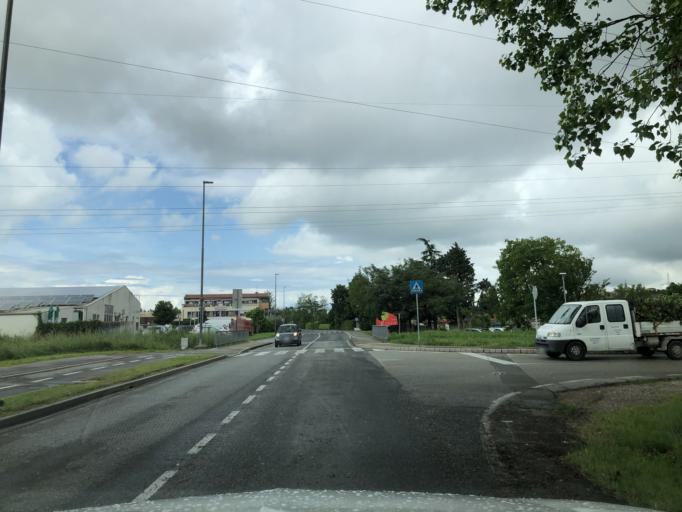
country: SI
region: Koper-Capodistria
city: Koper
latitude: 45.5274
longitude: 13.7401
